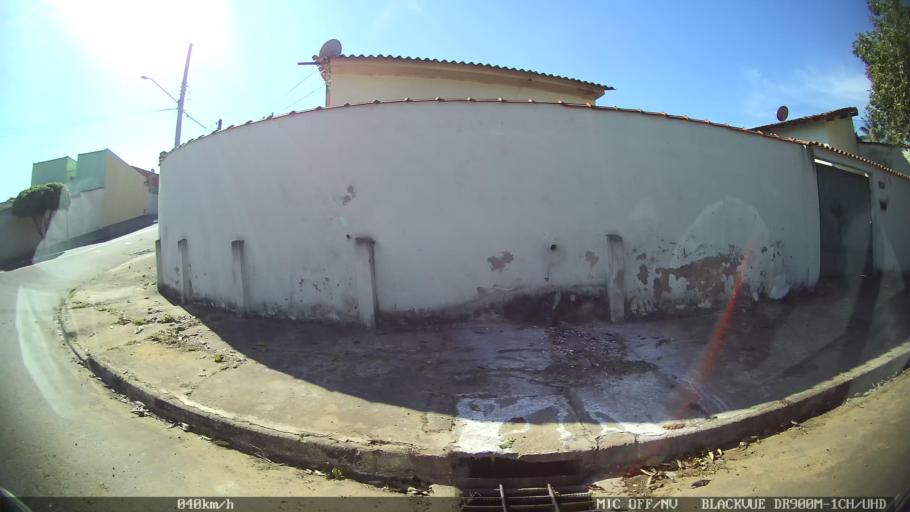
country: BR
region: Sao Paulo
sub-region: Franca
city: Franca
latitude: -20.4912
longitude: -47.4203
